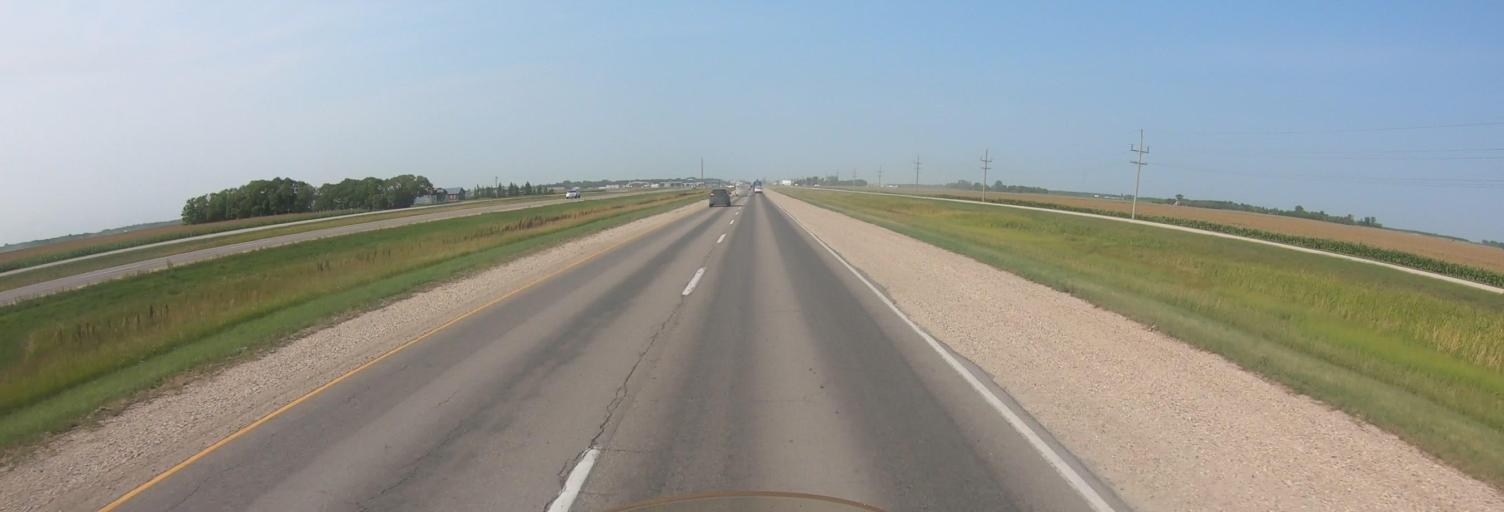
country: CA
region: Manitoba
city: Steinbach
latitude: 49.5854
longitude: -96.6875
